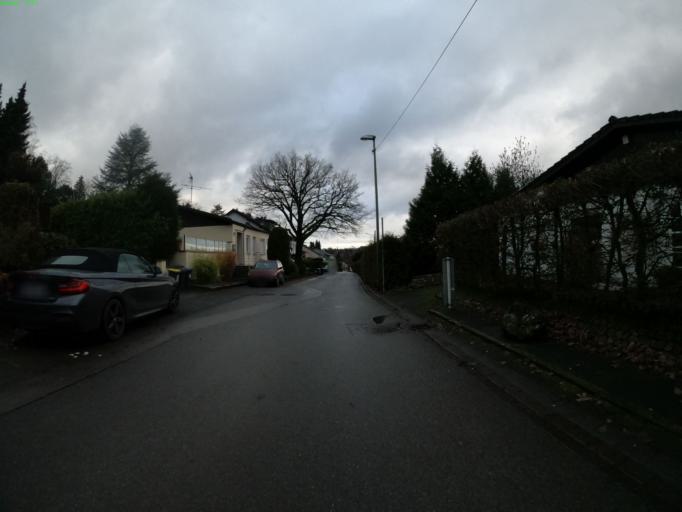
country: DE
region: North Rhine-Westphalia
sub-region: Regierungsbezirk Dusseldorf
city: Remscheid
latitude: 51.1836
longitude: 7.1390
